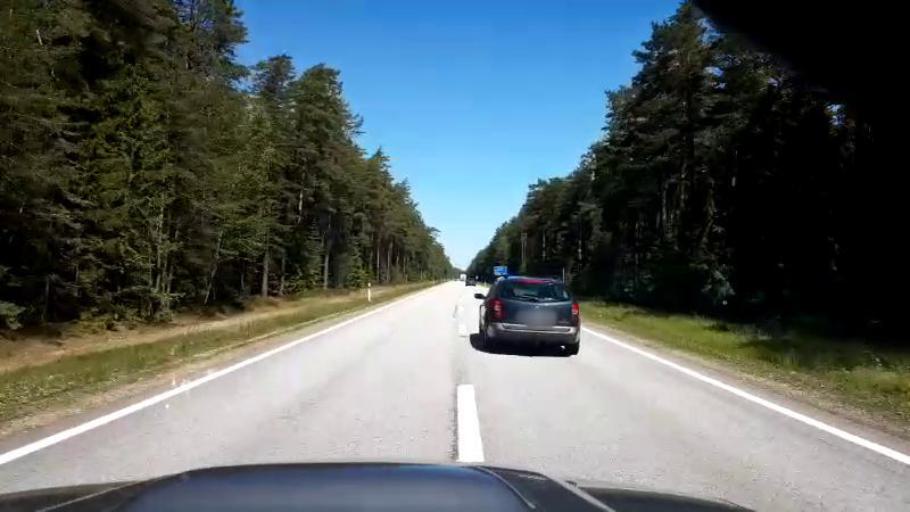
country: LV
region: Salacgrivas
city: Salacgriva
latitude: 57.5199
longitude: 24.4307
